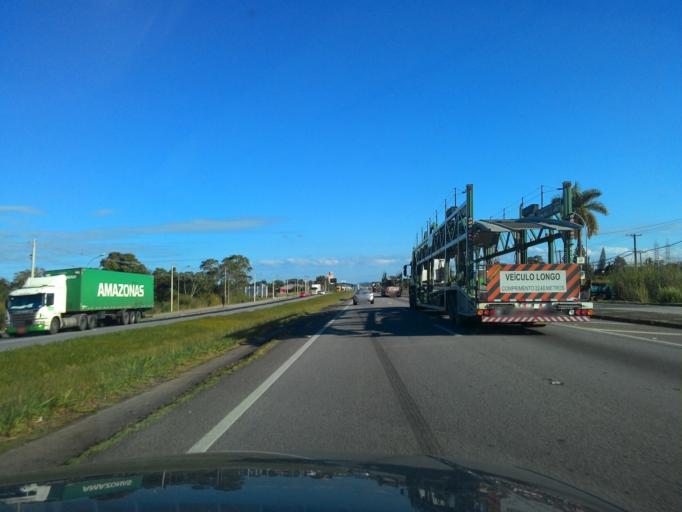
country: BR
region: Sao Paulo
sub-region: Registro
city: Registro
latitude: -24.5183
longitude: -47.8528
